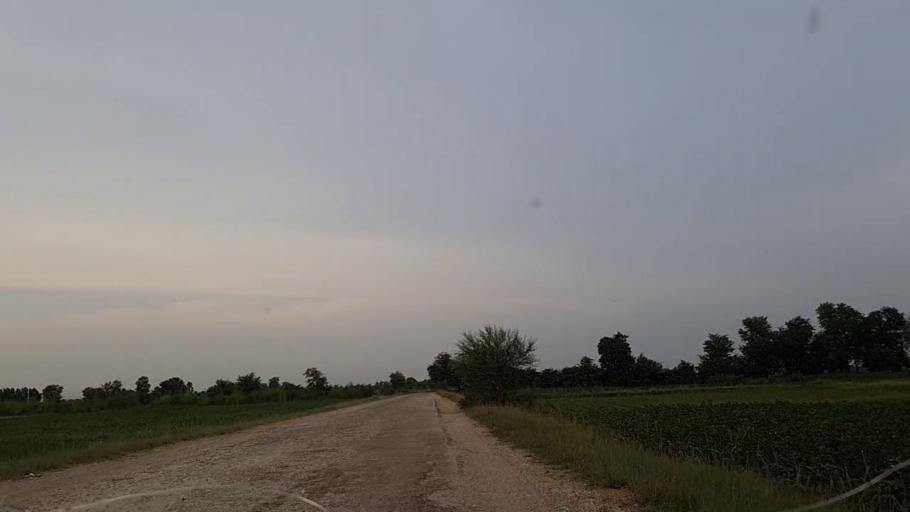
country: PK
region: Sindh
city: Mirpur Mathelo
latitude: 27.8767
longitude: 69.6367
